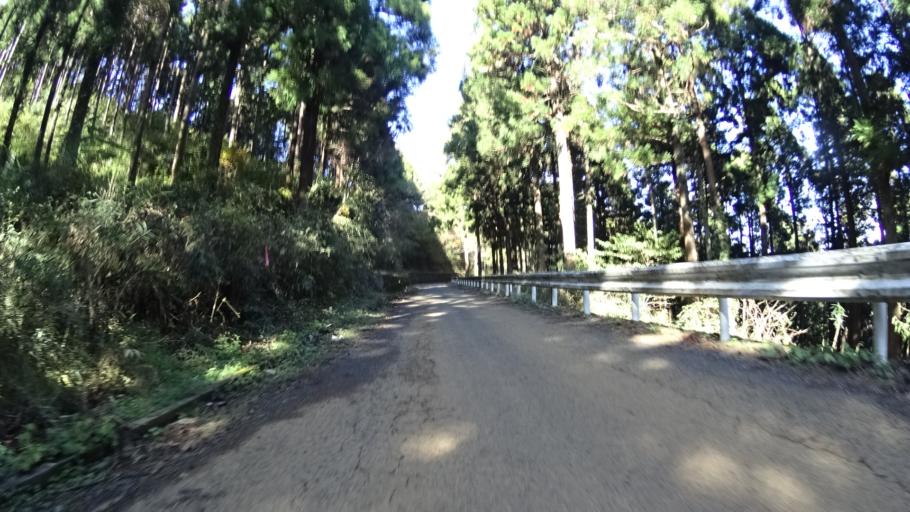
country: JP
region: Kanagawa
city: Zama
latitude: 35.5222
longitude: 139.2748
